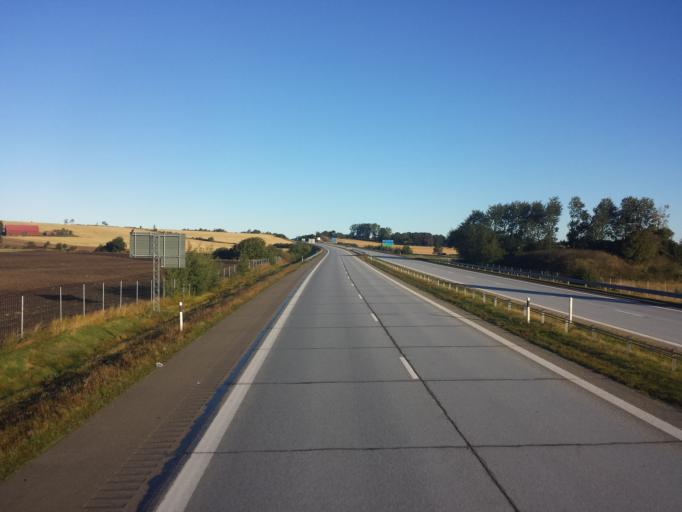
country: SE
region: Halland
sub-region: Falkenbergs Kommun
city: Falkenberg
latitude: 56.8908
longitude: 12.5976
